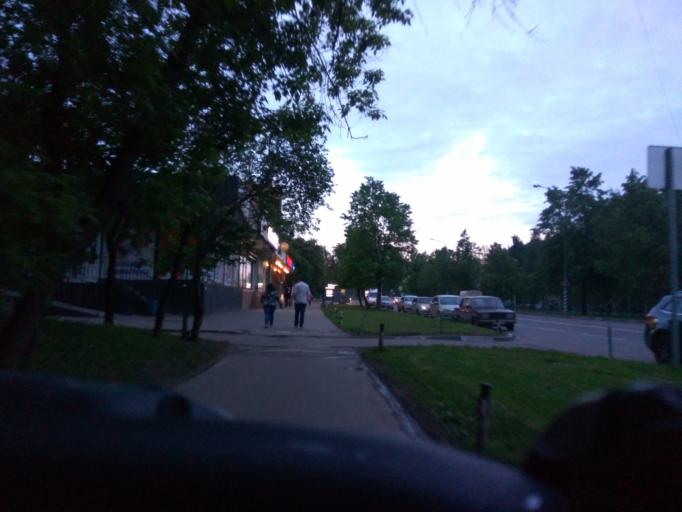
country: RU
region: Moscow
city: Kolomenskoye
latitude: 55.6689
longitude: 37.6487
